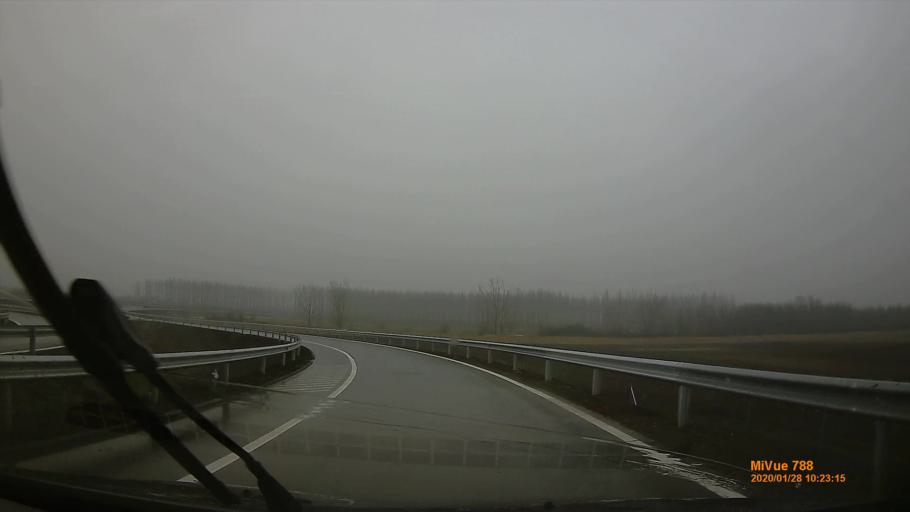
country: HU
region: Pest
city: Pilis
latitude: 47.3112
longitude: 19.5579
